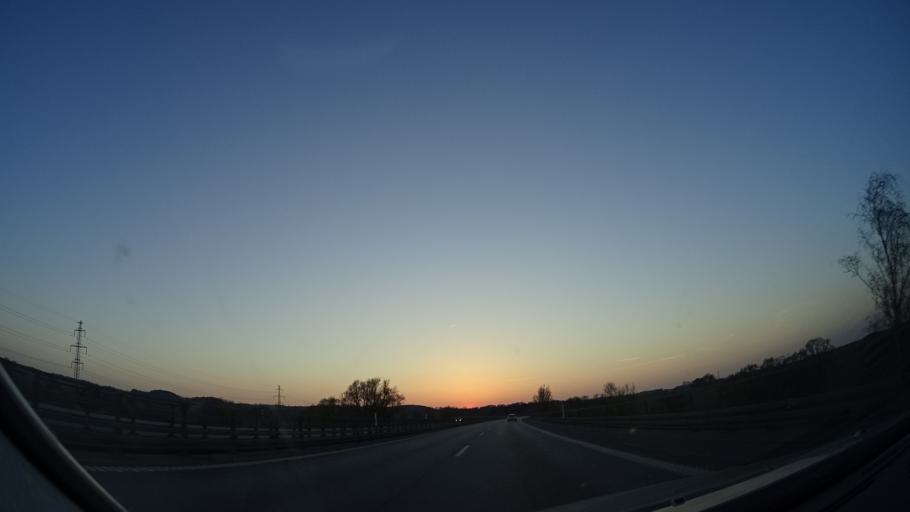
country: DK
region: Zealand
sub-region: Lejre Kommune
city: Lejre
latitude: 55.6235
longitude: 11.9784
